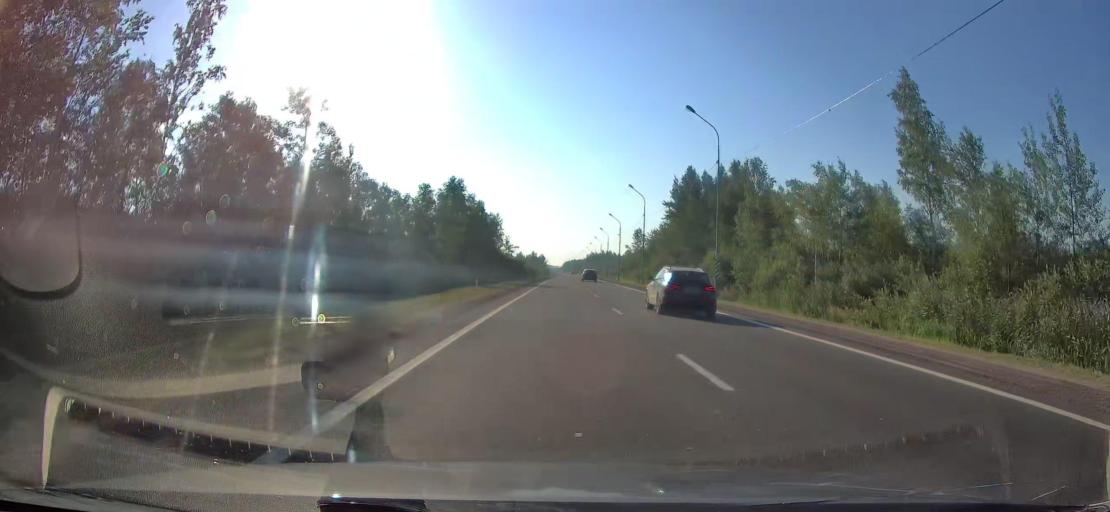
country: RU
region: Leningrad
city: Sinyavino
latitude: 59.9079
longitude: 31.0490
